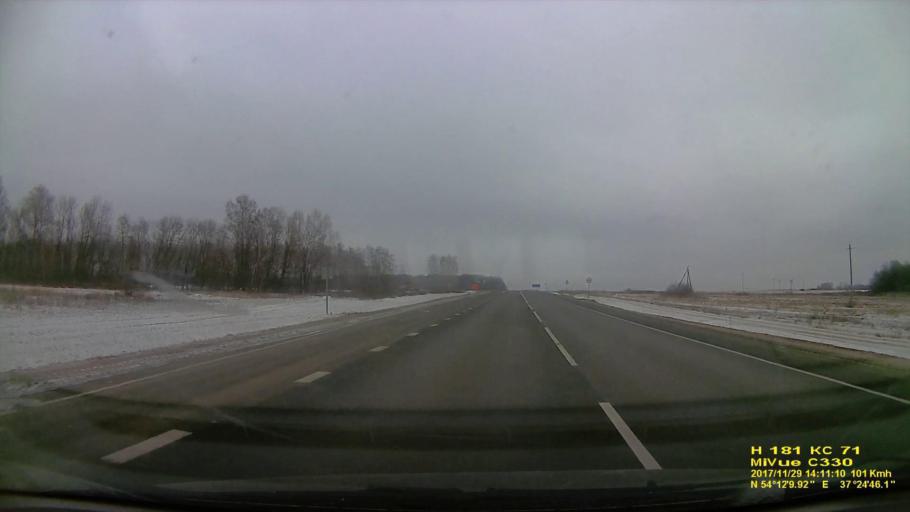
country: RU
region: Tula
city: Leninskiy
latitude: 54.2026
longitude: 37.4131
